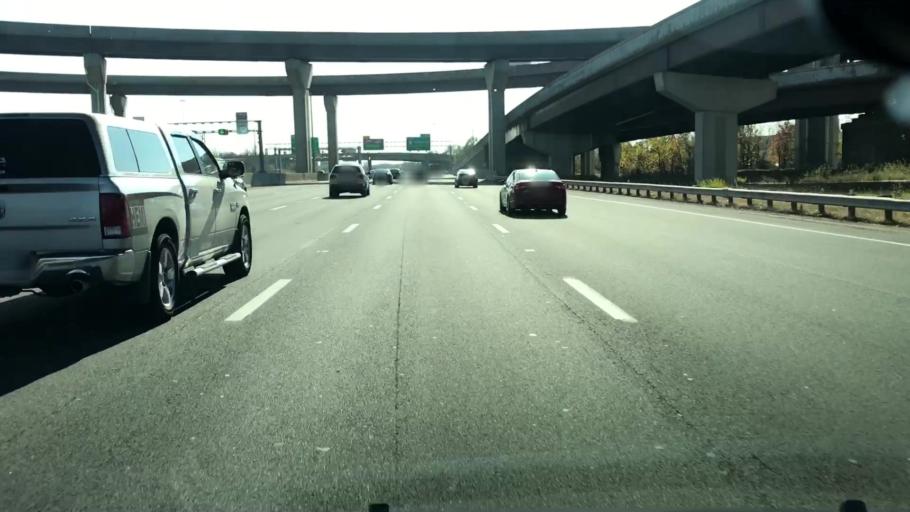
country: US
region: Virginia
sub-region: Fairfax County
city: Springfield
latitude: 38.7762
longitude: -77.1768
